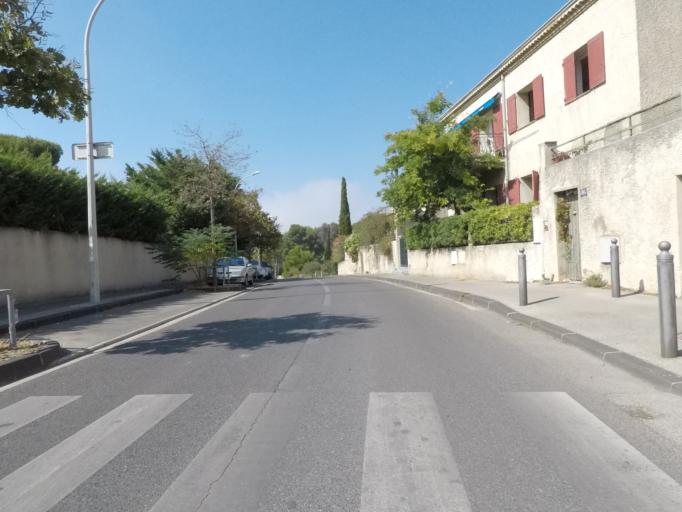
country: FR
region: Provence-Alpes-Cote d'Azur
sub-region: Departement des Bouches-du-Rhone
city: Marseille 09
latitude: 43.2561
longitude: 5.4283
